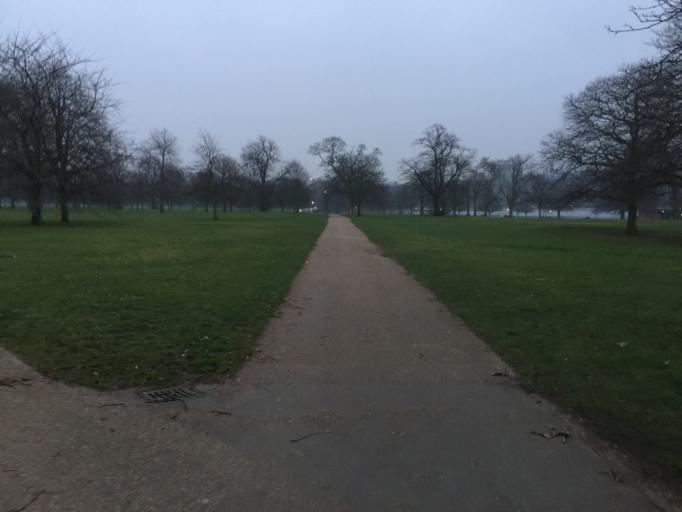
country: GB
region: England
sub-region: Greater London
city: Bayswater
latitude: 51.5080
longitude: -0.1640
